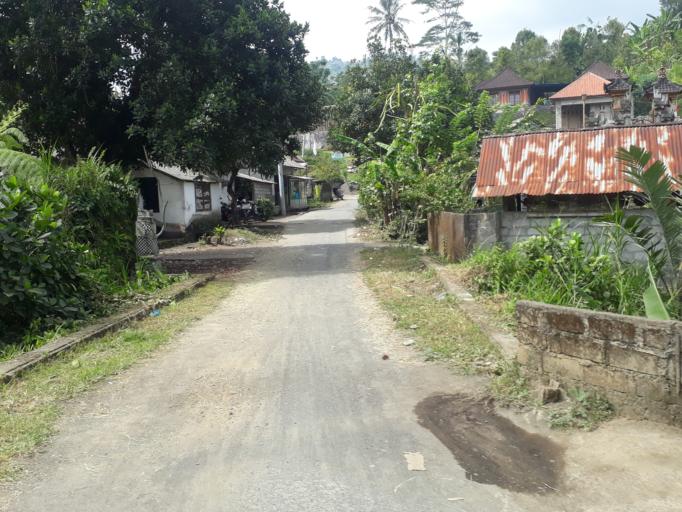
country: ID
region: Bali
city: Banjar Wangsian
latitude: -8.4574
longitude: 115.4414
